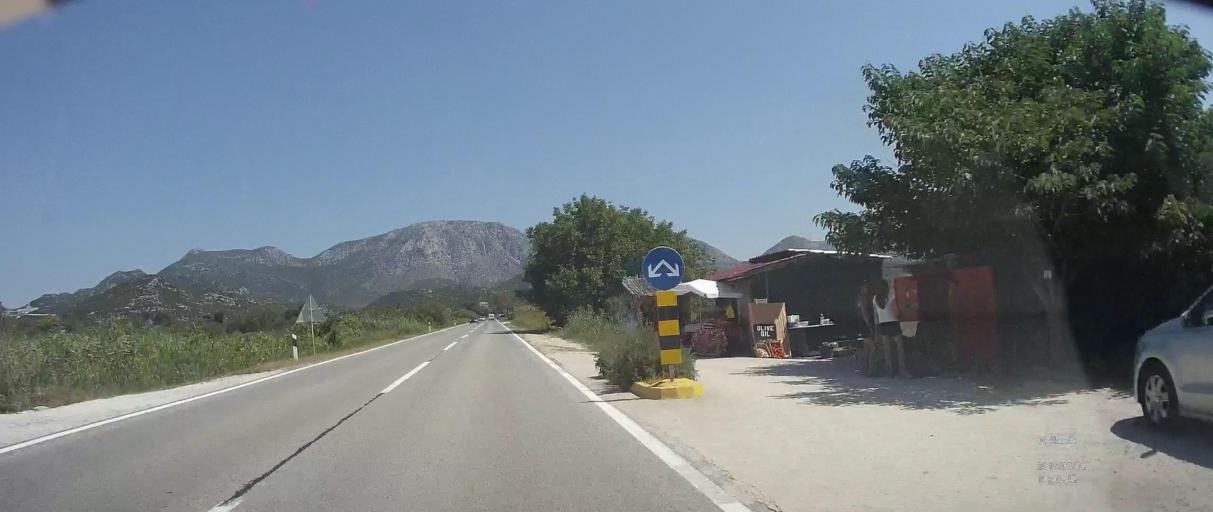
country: HR
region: Dubrovacko-Neretvanska
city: Komin
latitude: 43.0365
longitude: 17.4916
